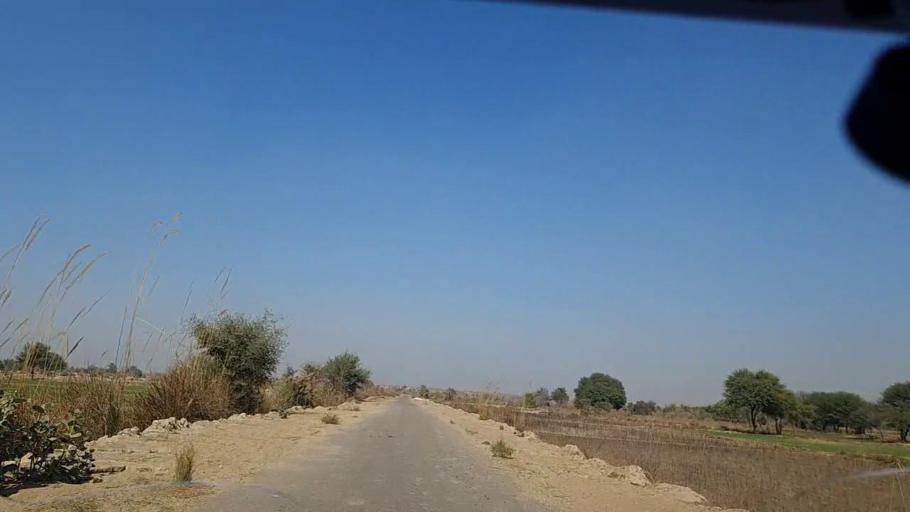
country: PK
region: Sindh
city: Khanpur
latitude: 27.5723
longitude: 69.3797
